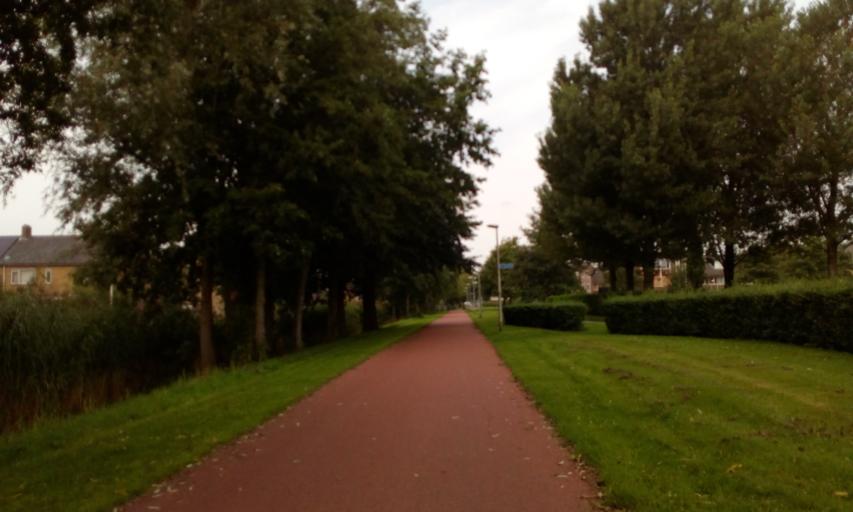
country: NL
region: South Holland
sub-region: Gemeente Den Haag
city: Ypenburg
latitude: 52.0485
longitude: 4.4027
